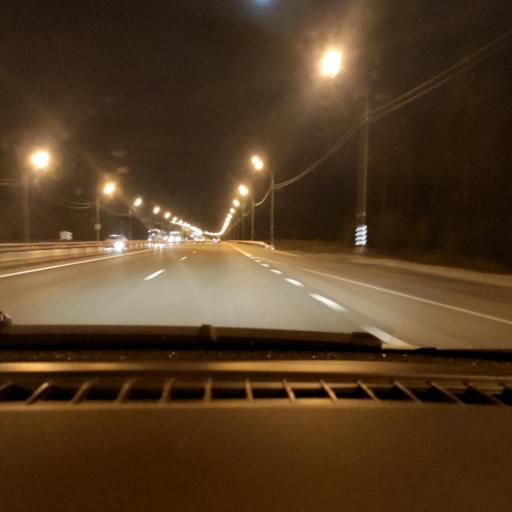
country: RU
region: Lipetsk
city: Khlevnoye
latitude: 52.2298
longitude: 39.0932
